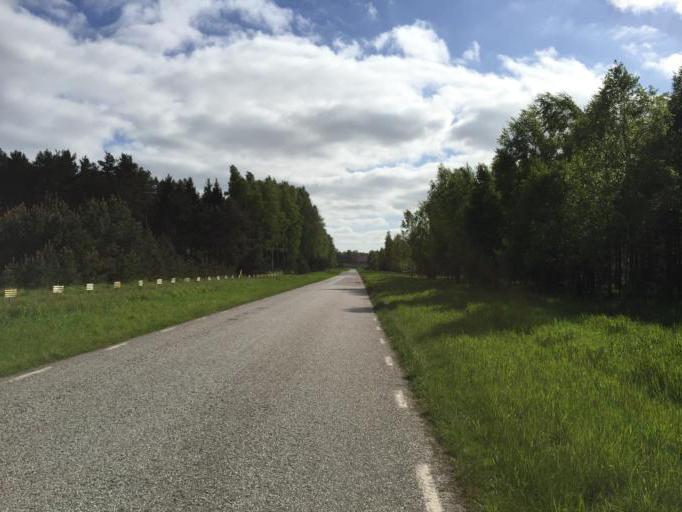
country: SE
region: Skane
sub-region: Sjobo Kommun
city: Blentarp
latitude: 55.6560
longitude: 13.6087
